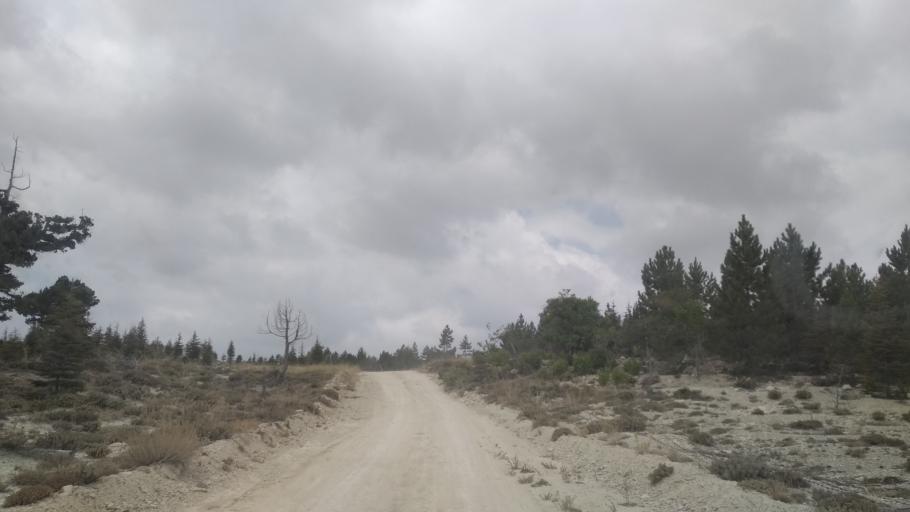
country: TR
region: Mersin
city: Sarikavak
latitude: 36.5742
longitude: 33.7597
